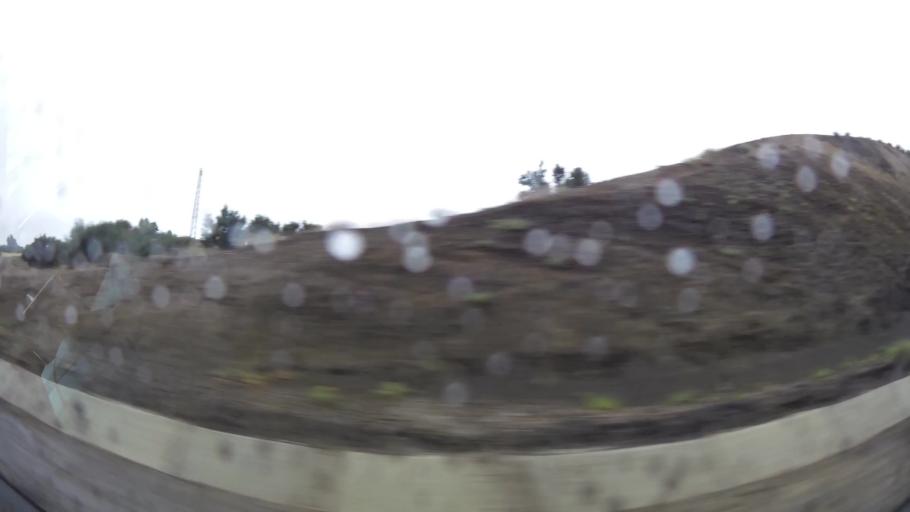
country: MA
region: Taza-Al Hoceima-Taounate
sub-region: Taza
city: Aknoul
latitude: 34.7964
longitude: -3.7454
